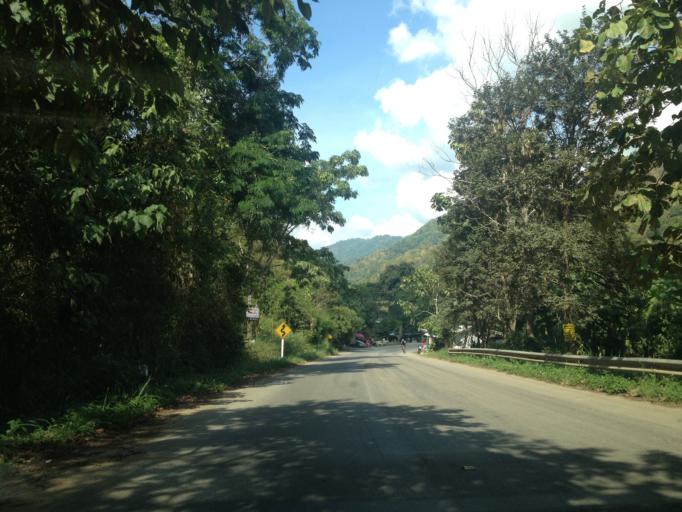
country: TH
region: Chiang Mai
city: Samoeng
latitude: 18.7917
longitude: 98.8368
